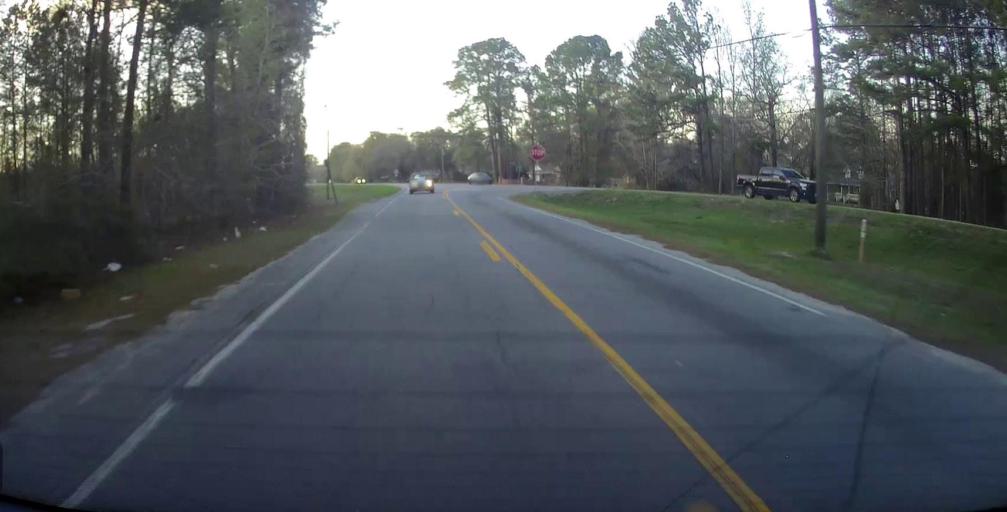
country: US
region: Georgia
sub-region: Chatham County
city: Bloomingdale
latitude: 32.1687
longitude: -81.3865
